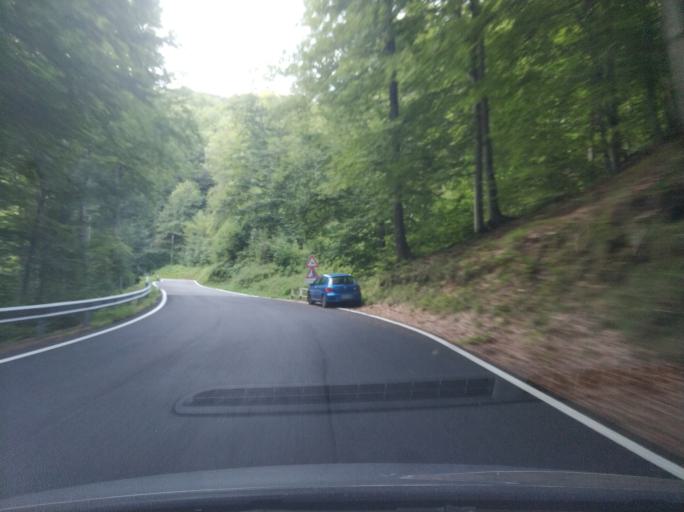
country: IT
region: Piedmont
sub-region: Provincia di Torino
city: Viu
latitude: 45.2239
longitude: 7.3826
